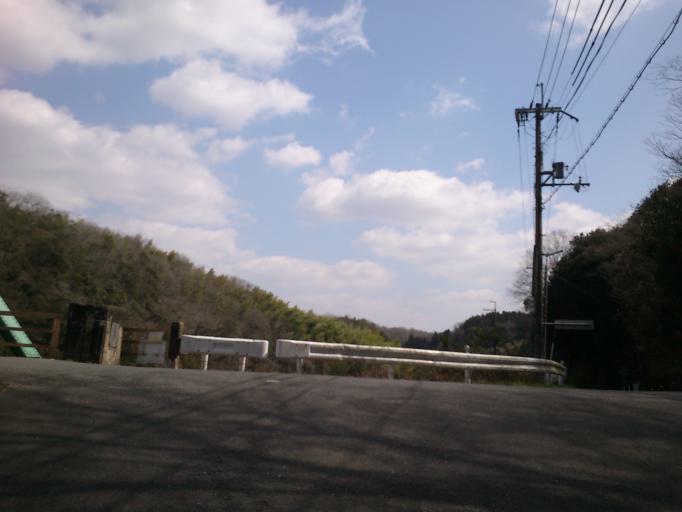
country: JP
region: Mie
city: Ueno-ebisumachi
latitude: 34.7600
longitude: 136.0214
